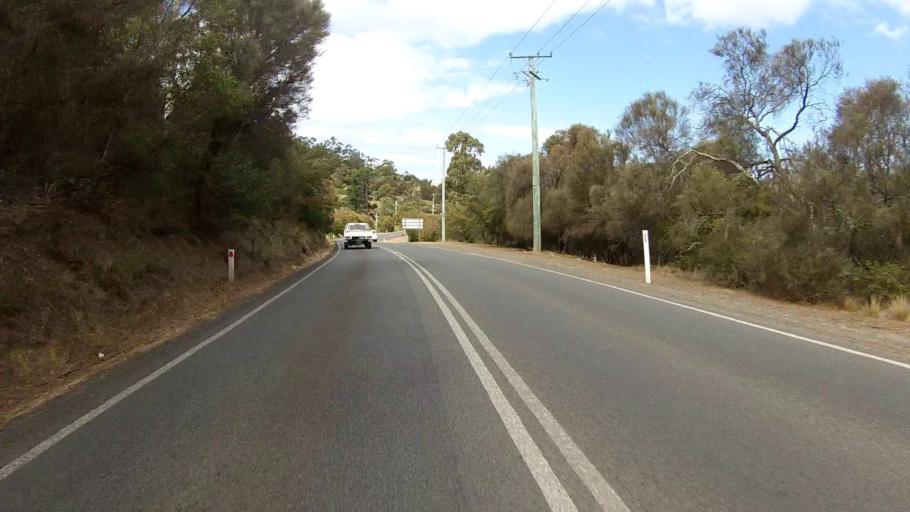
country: AU
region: Tasmania
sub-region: Clarence
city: Rokeby
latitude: -42.9071
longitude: 147.4591
